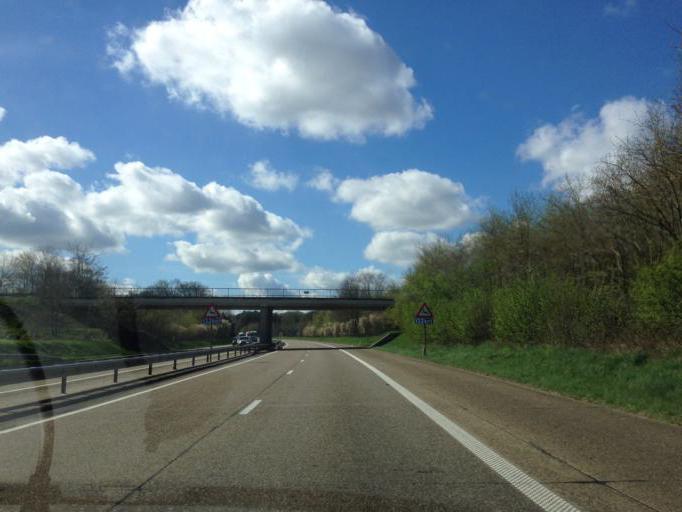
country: BE
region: Flanders
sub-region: Provincie Limburg
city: Helchteren
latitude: 51.1183
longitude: 5.3767
